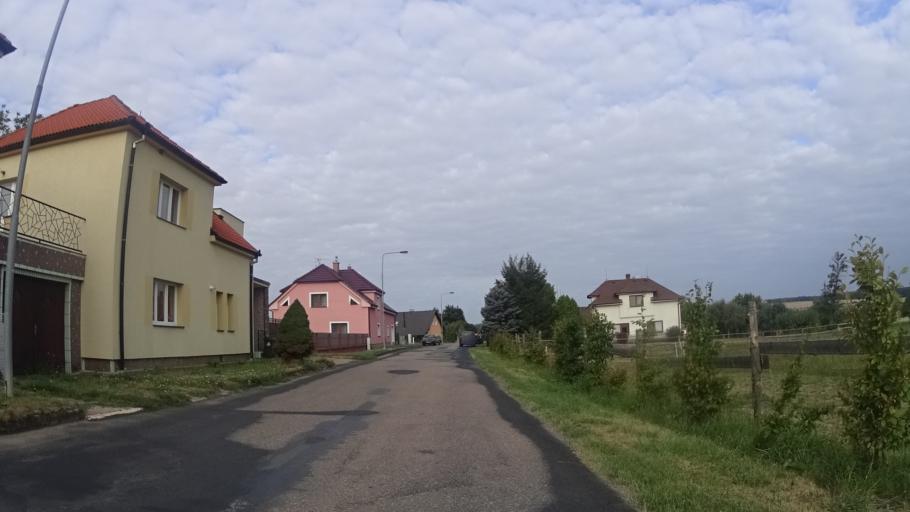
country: CZ
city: Stezery
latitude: 50.2089
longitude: 15.6994
